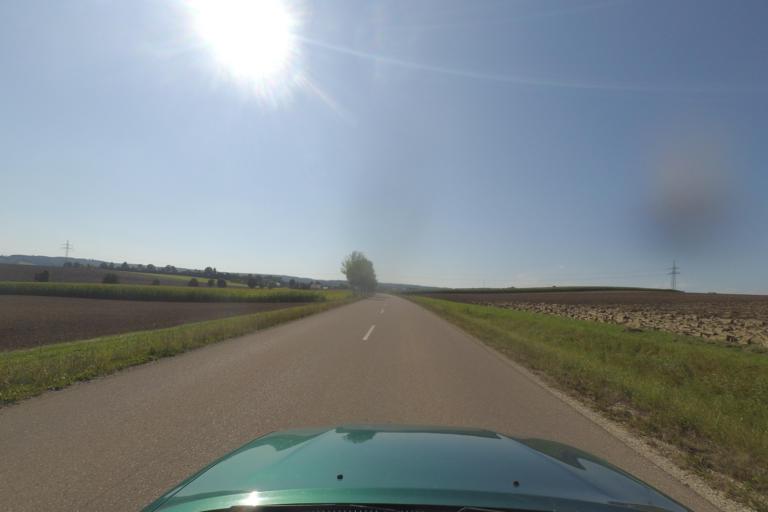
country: DE
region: Bavaria
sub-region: Swabia
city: Donauwoerth
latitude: 48.7337
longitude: 10.7357
